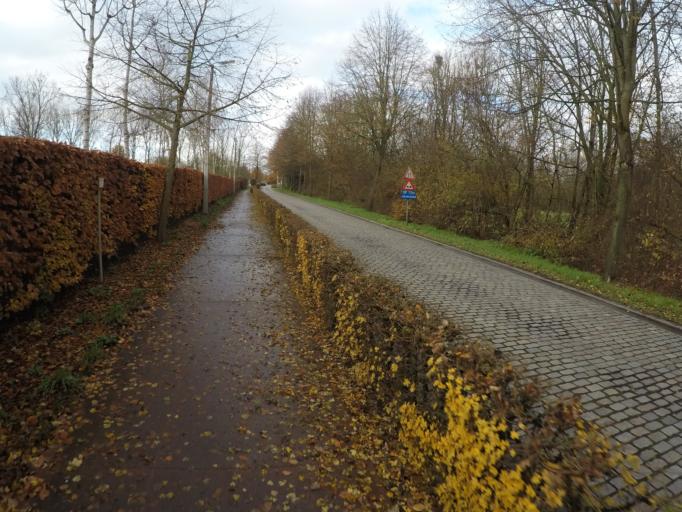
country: BE
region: Flanders
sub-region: Provincie Vlaams-Brabant
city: Londerzeel
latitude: 51.0014
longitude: 4.2733
